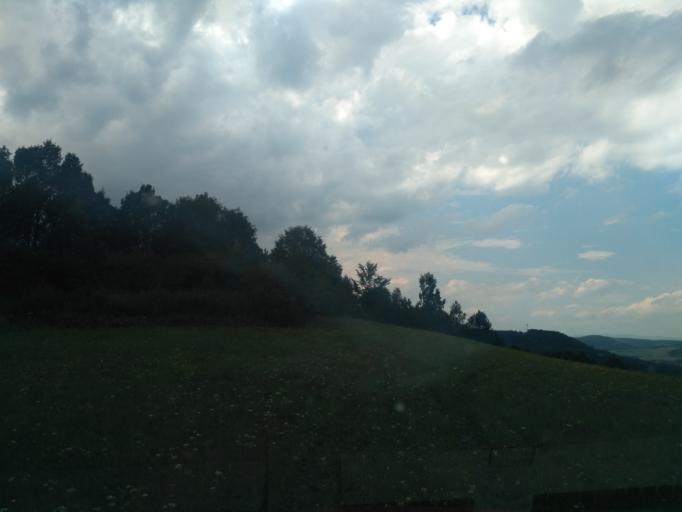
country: SK
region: Presovsky
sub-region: Okres Presov
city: Presov
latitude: 48.9169
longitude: 21.1846
